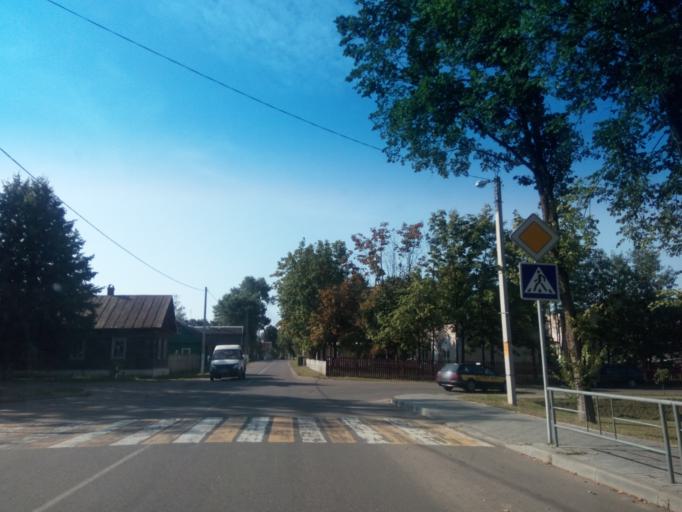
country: BY
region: Vitebsk
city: Vyerkhnyadzvinsk
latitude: 55.7754
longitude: 27.9318
